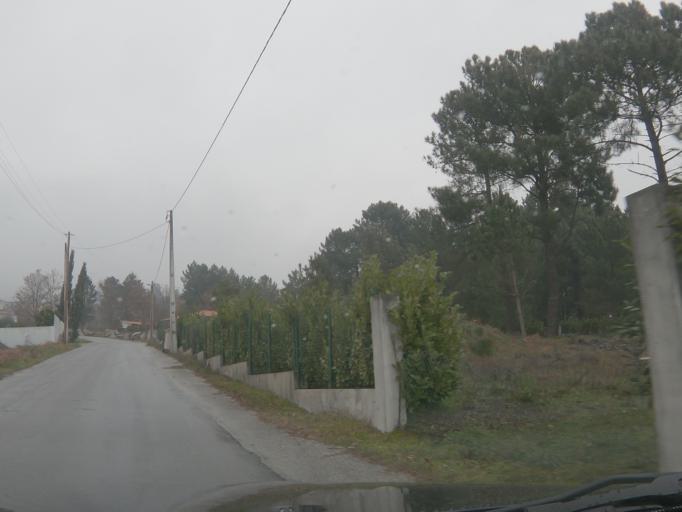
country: PT
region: Vila Real
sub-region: Vila Real
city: Vila Real
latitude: 41.3015
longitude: -7.7800
